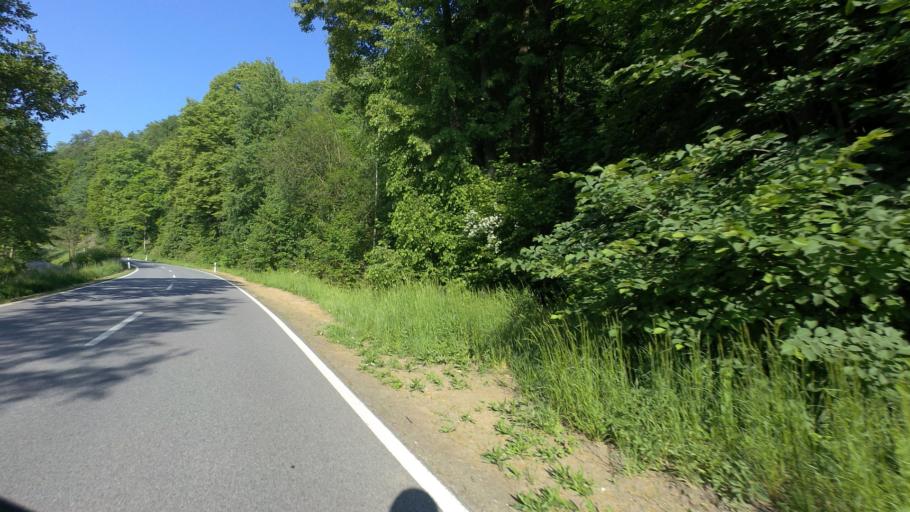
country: DE
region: Saxony
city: Sebnitz
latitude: 50.9685
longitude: 14.2359
